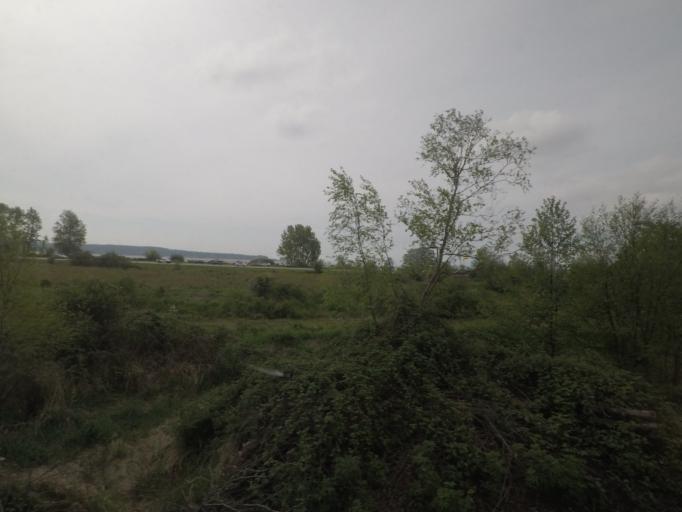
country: CA
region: British Columbia
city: Delta
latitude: 49.0931
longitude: -122.8876
